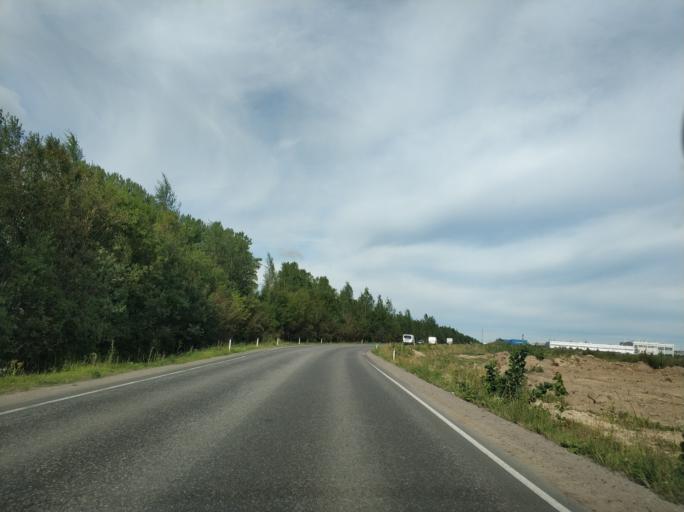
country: RU
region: St.-Petersburg
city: Grazhdanka
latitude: 60.0450
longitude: 30.4247
